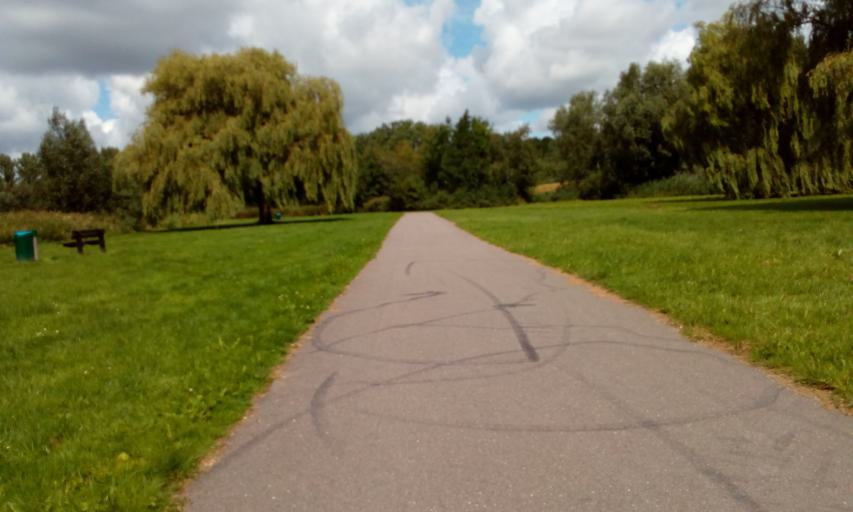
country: NL
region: South Holland
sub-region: Gemeente Barendrecht
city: Barendrecht
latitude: 51.8672
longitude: 4.5019
